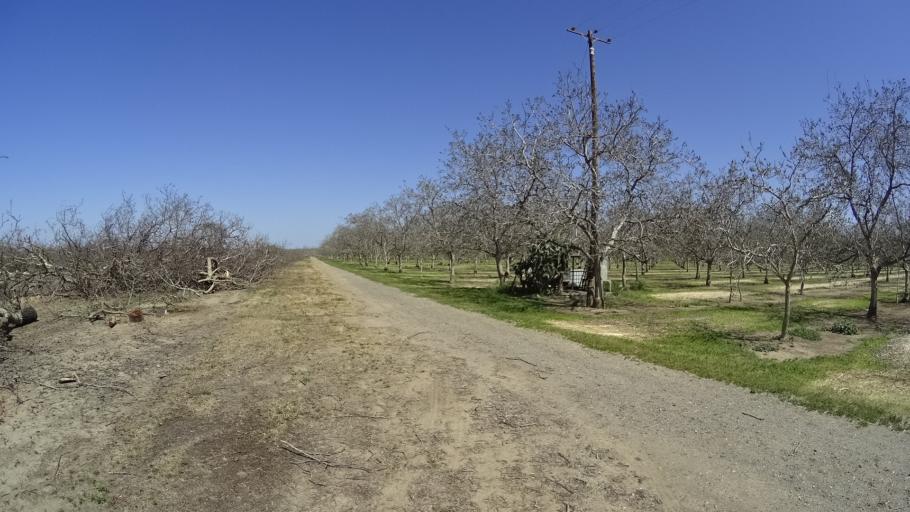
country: US
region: California
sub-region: Glenn County
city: Willows
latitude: 39.4463
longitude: -121.9823
